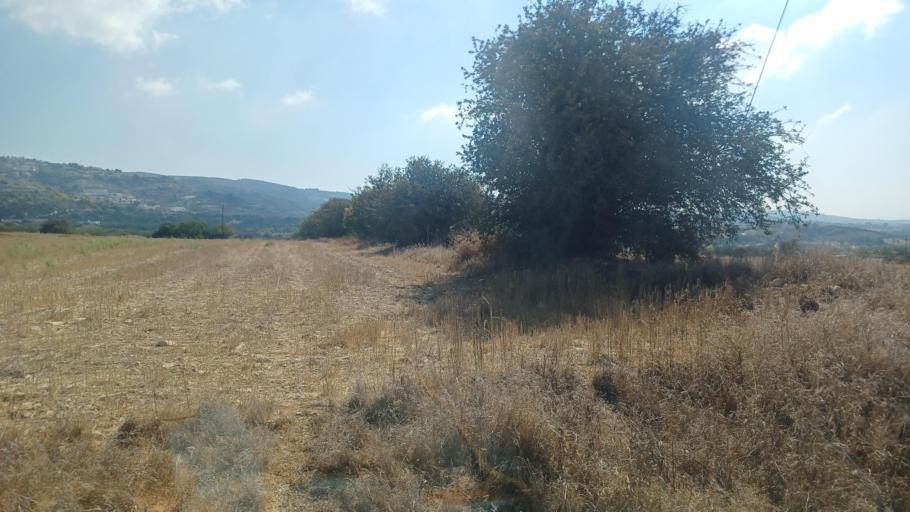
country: CY
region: Pafos
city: Mesogi
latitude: 34.8305
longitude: 32.4542
